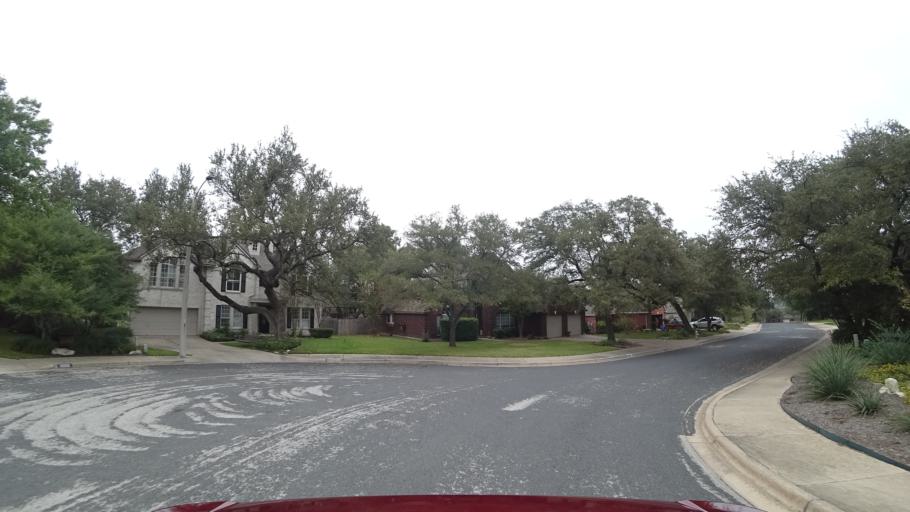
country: US
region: Texas
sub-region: Williamson County
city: Anderson Mill
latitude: 30.4357
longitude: -97.8215
